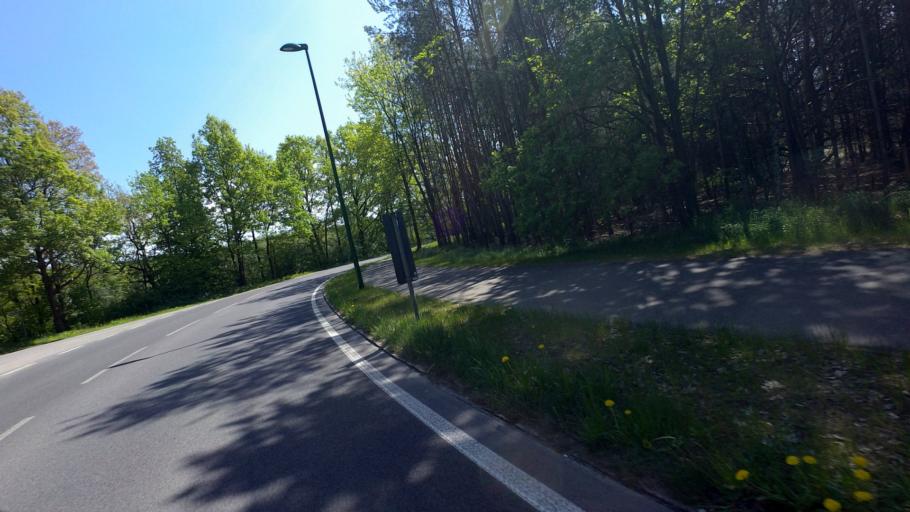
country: DE
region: Brandenburg
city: Bestensee
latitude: 52.2621
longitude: 13.6355
